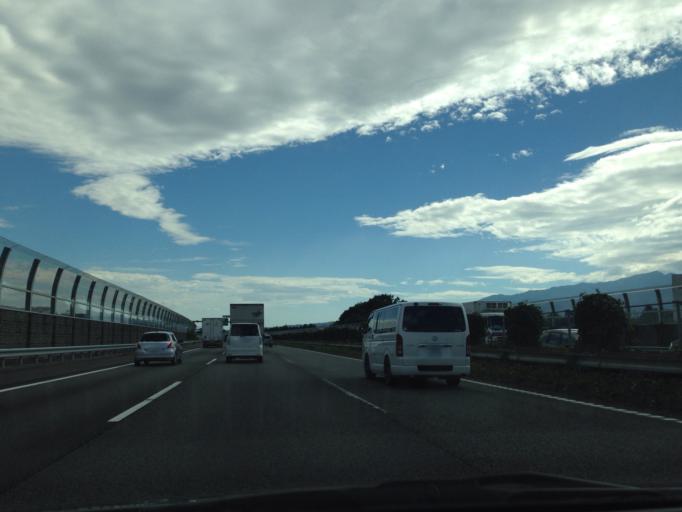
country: JP
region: Shizuoka
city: Gotemba
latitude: 35.2772
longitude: 138.9192
